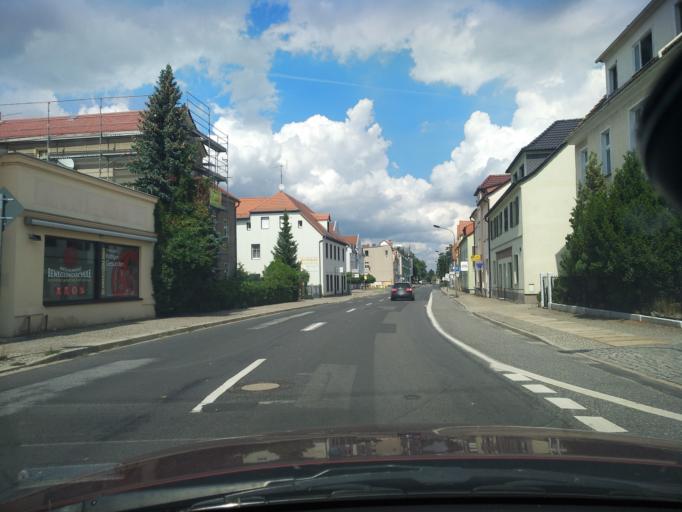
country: DE
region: Saxony
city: Niesky
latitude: 51.2901
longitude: 14.8211
